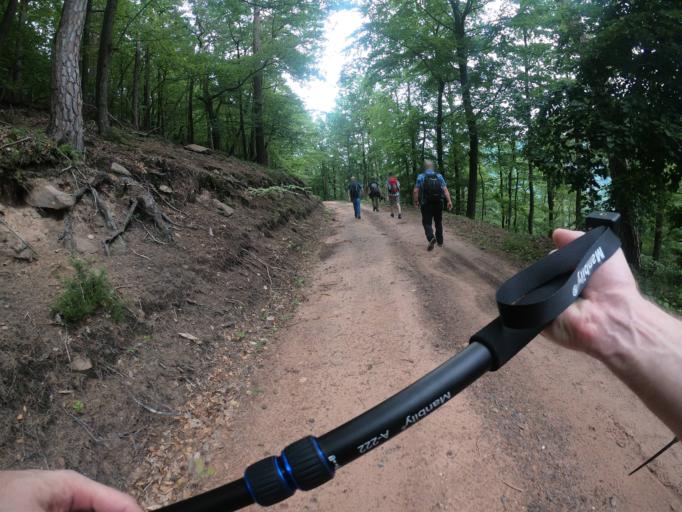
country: DE
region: Rheinland-Pfalz
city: Leinsweiler
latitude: 49.1893
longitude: 7.9961
